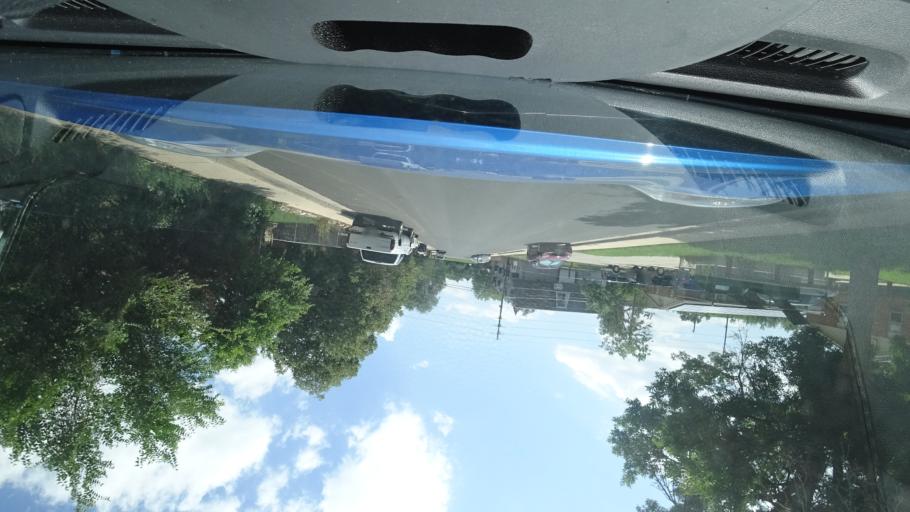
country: US
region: Colorado
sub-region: Arapahoe County
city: Sheridan
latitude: 39.6621
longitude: -105.0231
